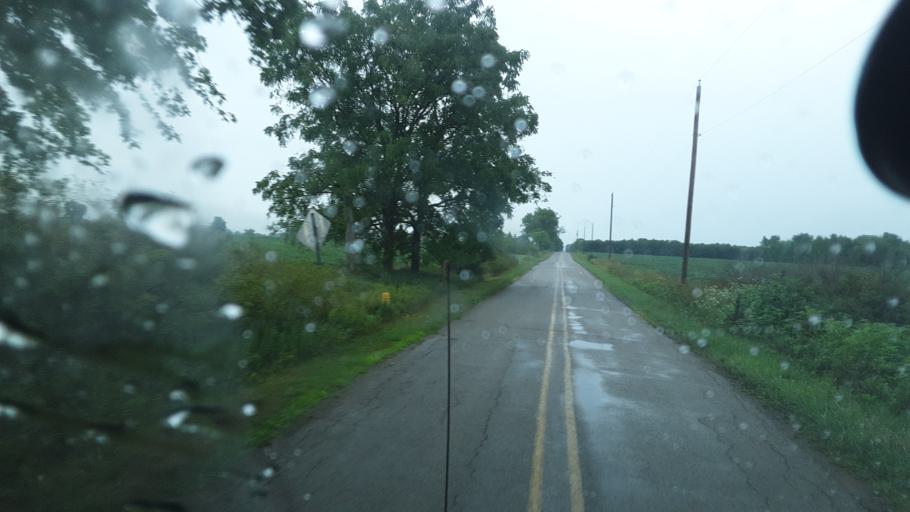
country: US
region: Indiana
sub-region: Steuben County
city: Hamilton
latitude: 41.5287
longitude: -84.8158
